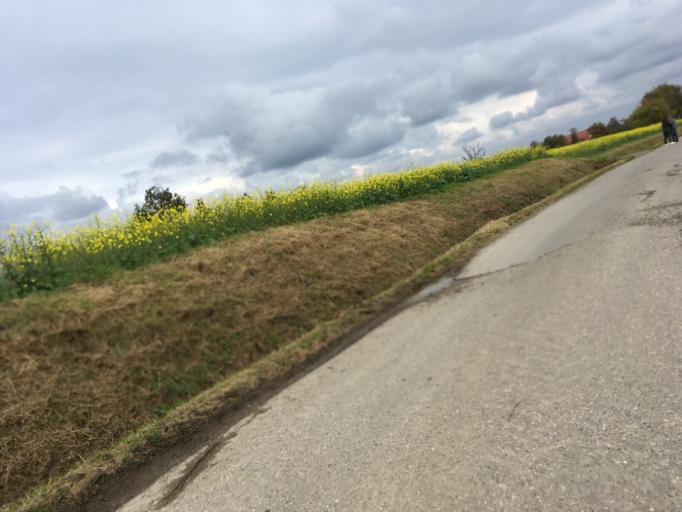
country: DE
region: Baden-Wuerttemberg
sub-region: Tuebingen Region
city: Kusterdingen
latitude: 48.4945
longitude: 9.0937
